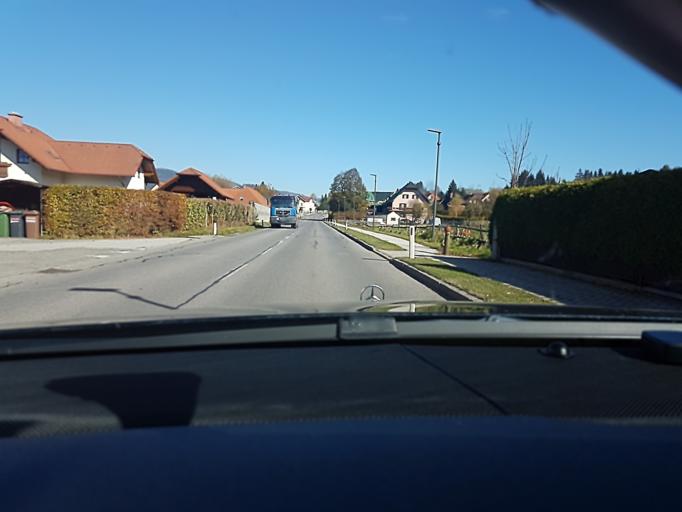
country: AT
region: Styria
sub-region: Politischer Bezirk Bruck-Muerzzuschlag
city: Mitterdorf im Muerztal
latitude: 47.5342
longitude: 15.5154
